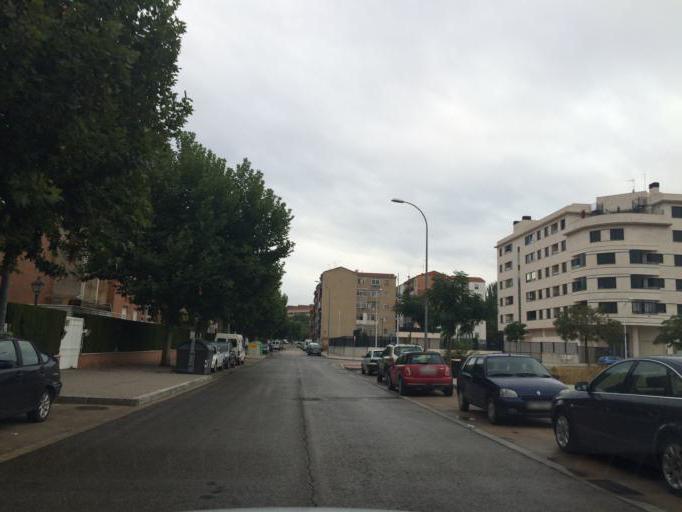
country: ES
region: Castille-La Mancha
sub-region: Provincia de Albacete
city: Albacete
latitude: 39.0050
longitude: -1.8561
